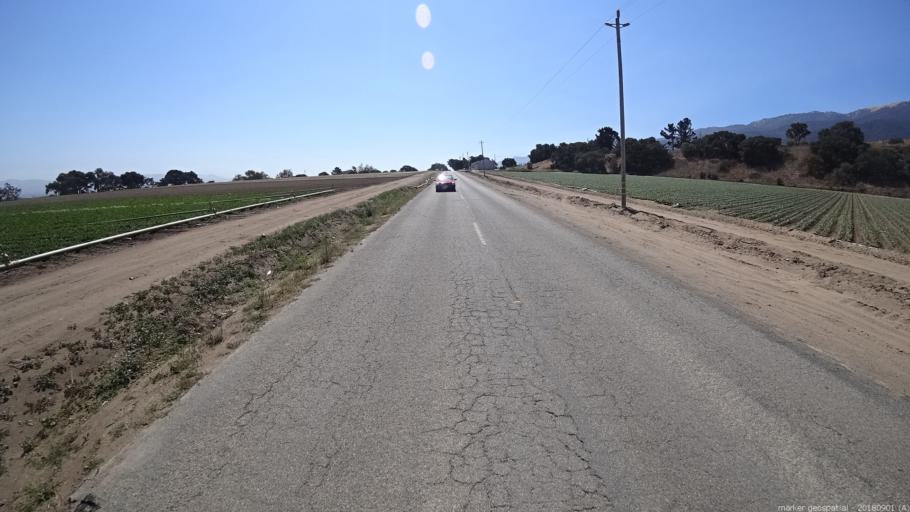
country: US
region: California
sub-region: Monterey County
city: Chualar
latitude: 36.5251
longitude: -121.5245
